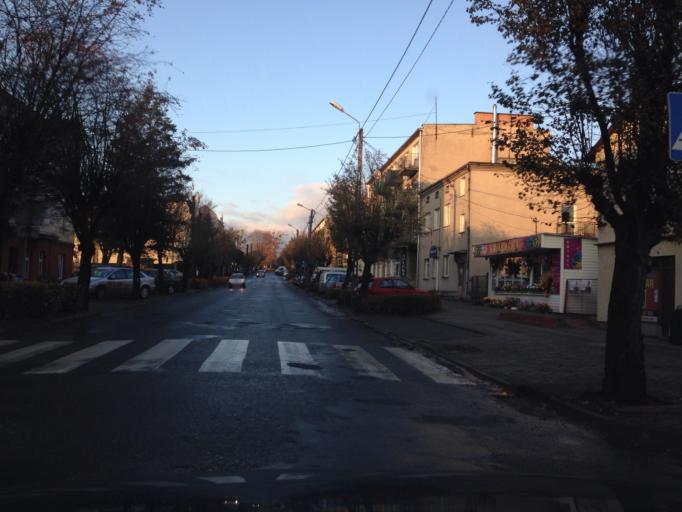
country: PL
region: Kujawsko-Pomorskie
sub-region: Powiat brodnicki
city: Jablonowo Pomorskie
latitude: 53.3889
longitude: 19.1544
